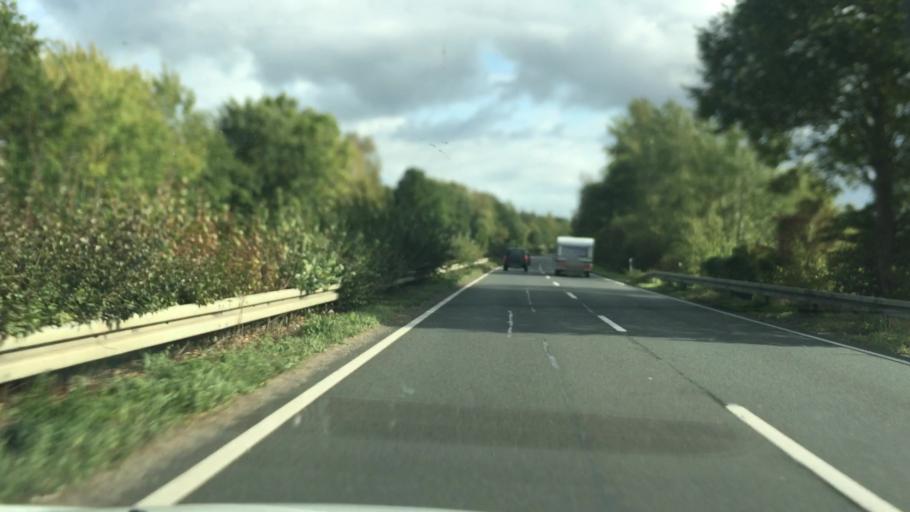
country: DE
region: Lower Saxony
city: Neustadt am Rubenberge
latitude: 52.4961
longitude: 9.4805
